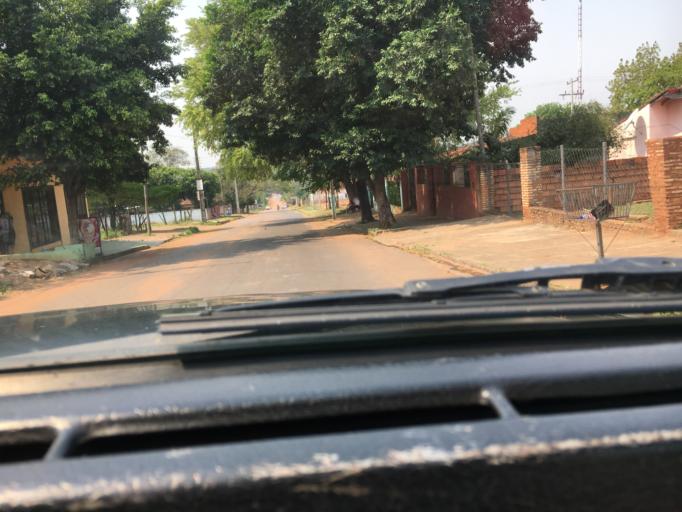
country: PY
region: Central
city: Villa Elisa
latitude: -25.3838
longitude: -57.5757
